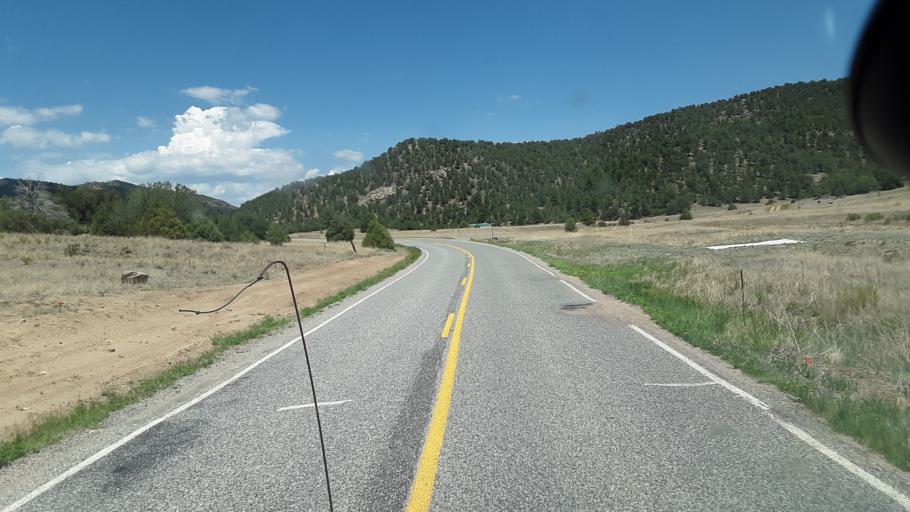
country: US
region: Colorado
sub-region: Fremont County
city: Canon City
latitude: 38.3718
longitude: -105.4575
